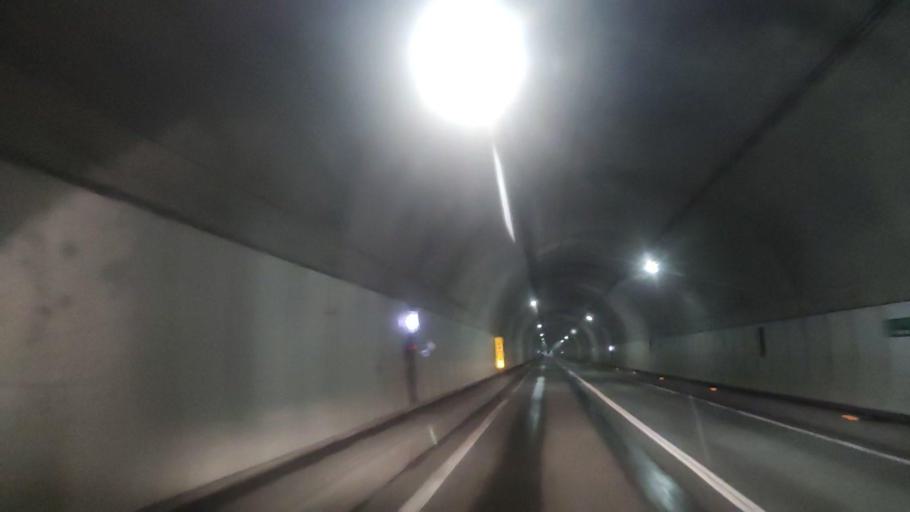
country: JP
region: Hokkaido
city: Date
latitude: 42.5542
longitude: 141.0737
